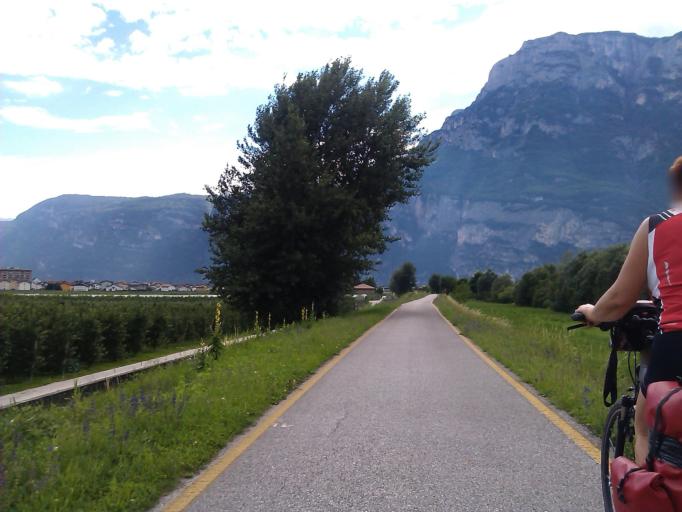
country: IT
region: Trentino-Alto Adige
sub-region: Provincia di Trento
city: Nave San Rocco
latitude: 46.1605
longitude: 11.1035
